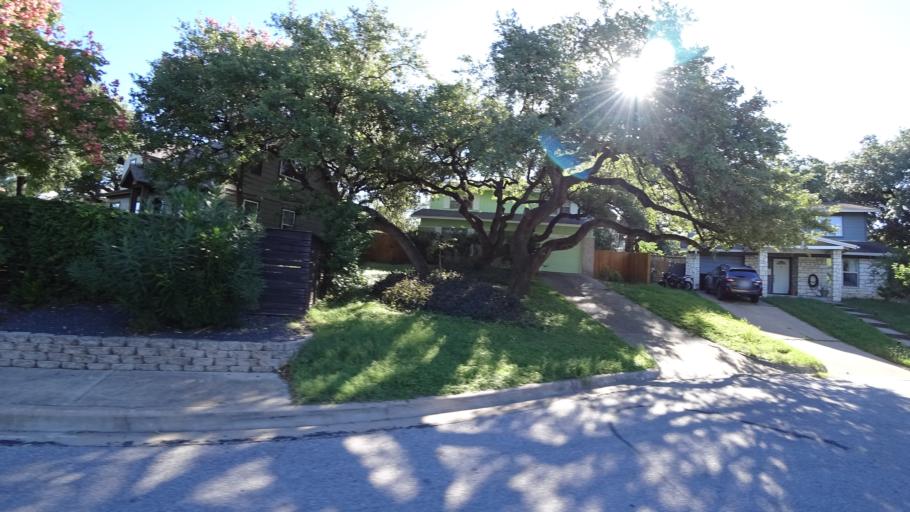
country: US
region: Texas
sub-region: Travis County
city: Austin
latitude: 30.2339
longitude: -97.7592
